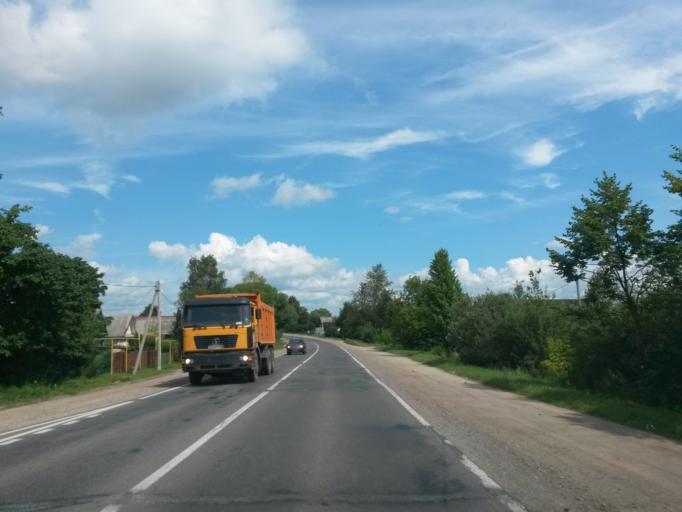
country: RU
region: Jaroslavl
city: Pereslavl'-Zalesskiy
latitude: 56.7640
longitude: 38.8720
